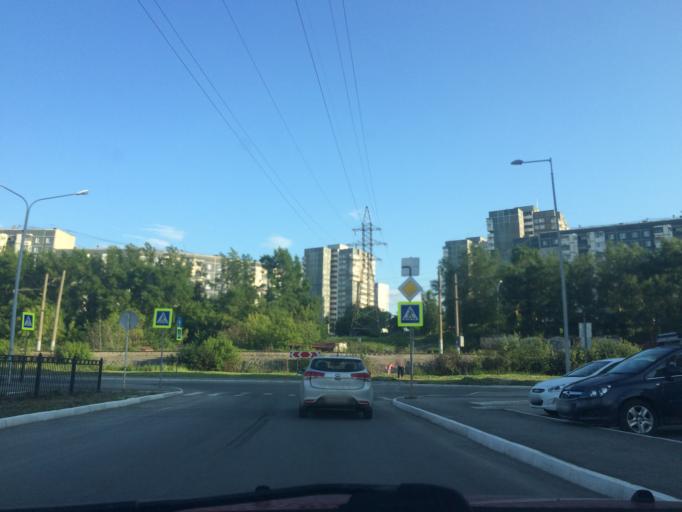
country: RU
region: Sverdlovsk
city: Yekaterinburg
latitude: 56.8292
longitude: 60.6747
